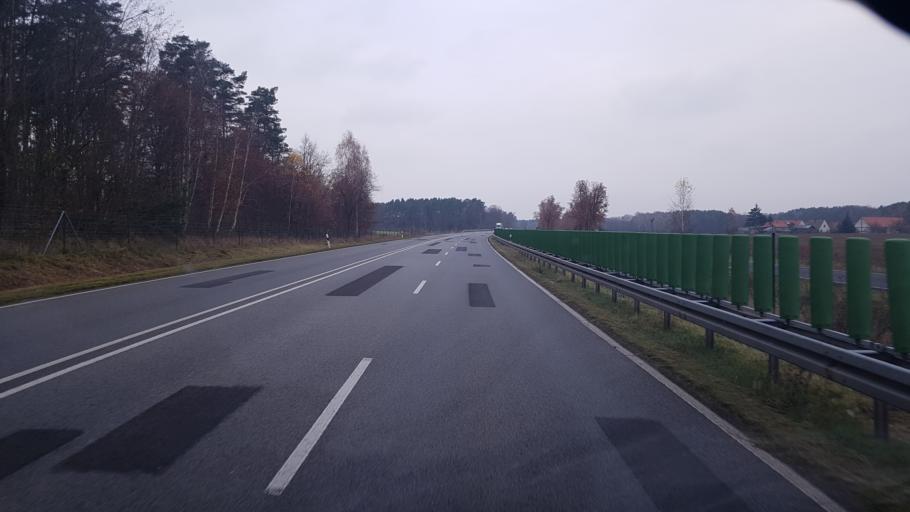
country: DE
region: Brandenburg
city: Neuzelle
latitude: 52.0470
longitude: 14.6732
